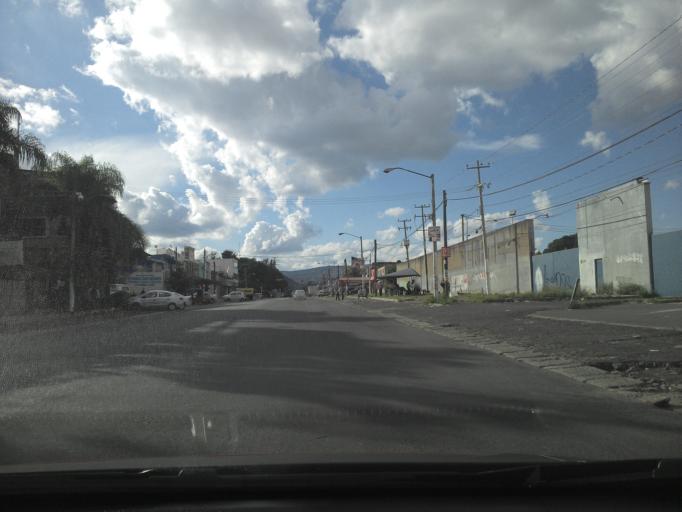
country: MX
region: Jalisco
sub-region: Tlajomulco de Zuniga
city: La Tijera
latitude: 20.6126
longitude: -103.4293
